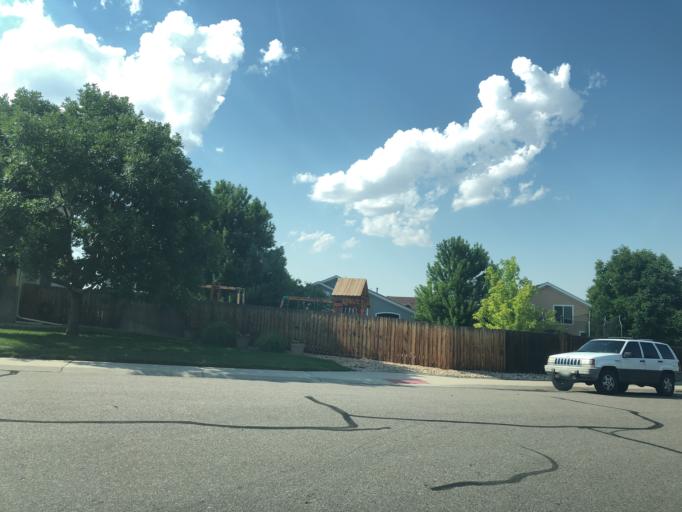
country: US
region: Colorado
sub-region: Arapahoe County
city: Dove Valley
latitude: 39.6351
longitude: -104.7531
